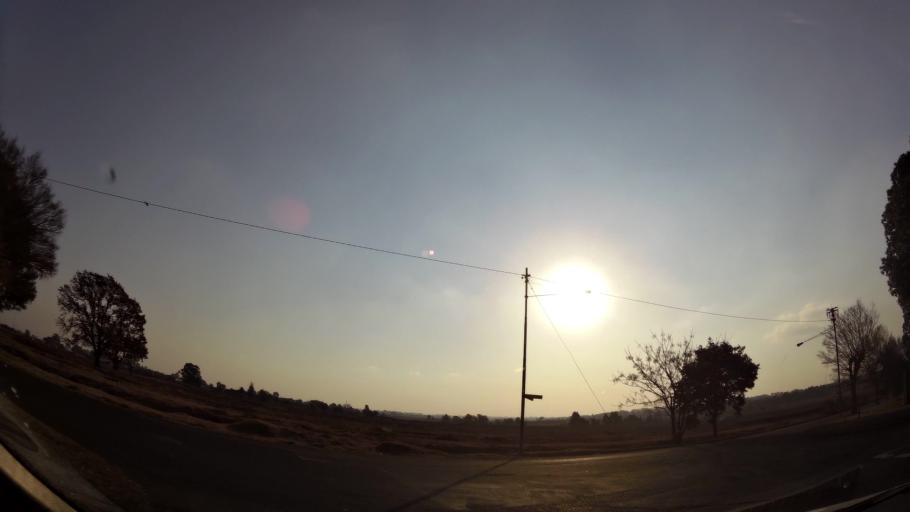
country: ZA
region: Gauteng
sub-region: Ekurhuleni Metropolitan Municipality
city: Springs
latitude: -26.2922
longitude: 28.4404
